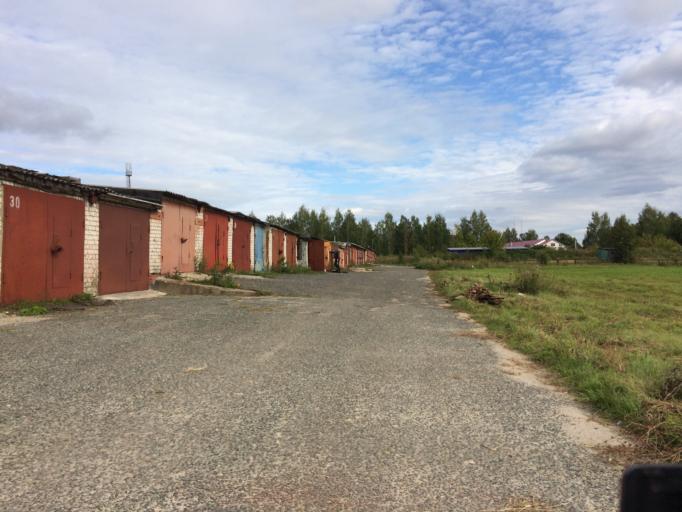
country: RU
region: Mariy-El
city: Yoshkar-Ola
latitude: 56.6504
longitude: 47.9619
